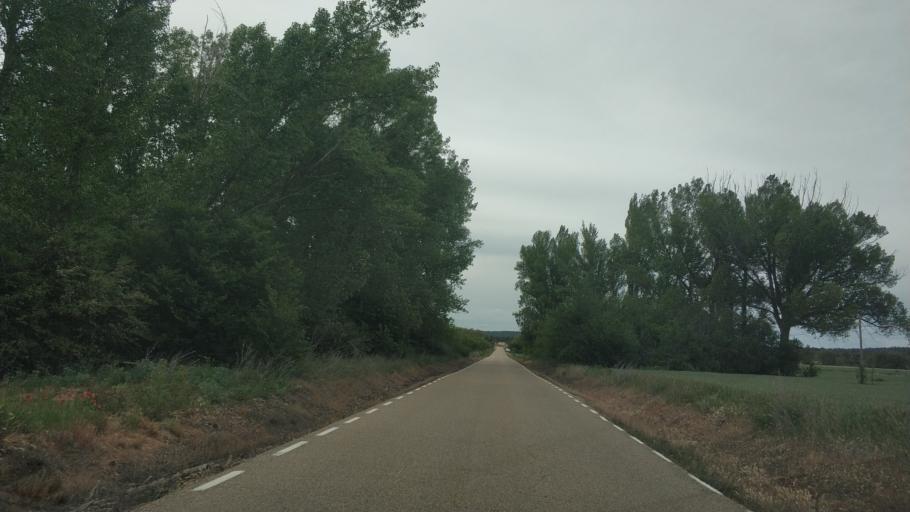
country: ES
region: Castille and Leon
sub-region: Provincia de Soria
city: Berlanga de Duero
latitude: 41.4885
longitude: -2.8668
